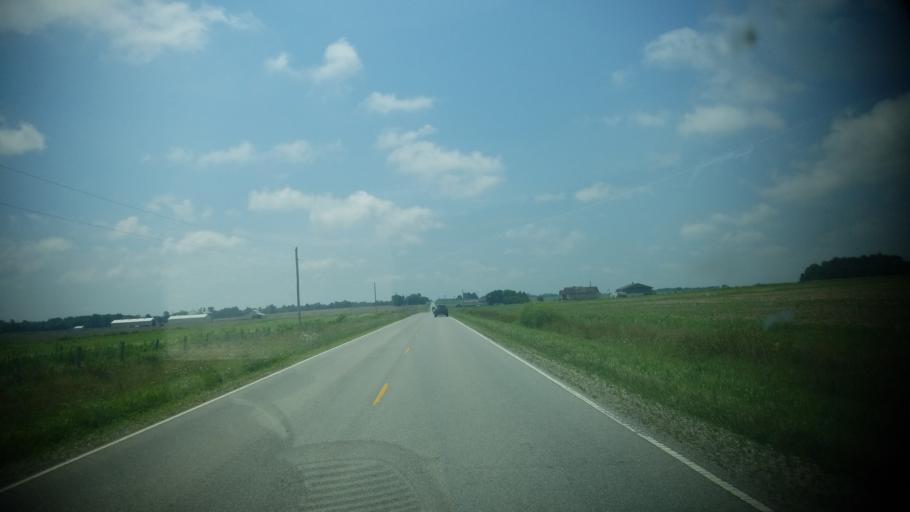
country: US
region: Illinois
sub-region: Wayne County
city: Fairfield
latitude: 38.4506
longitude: -88.3491
